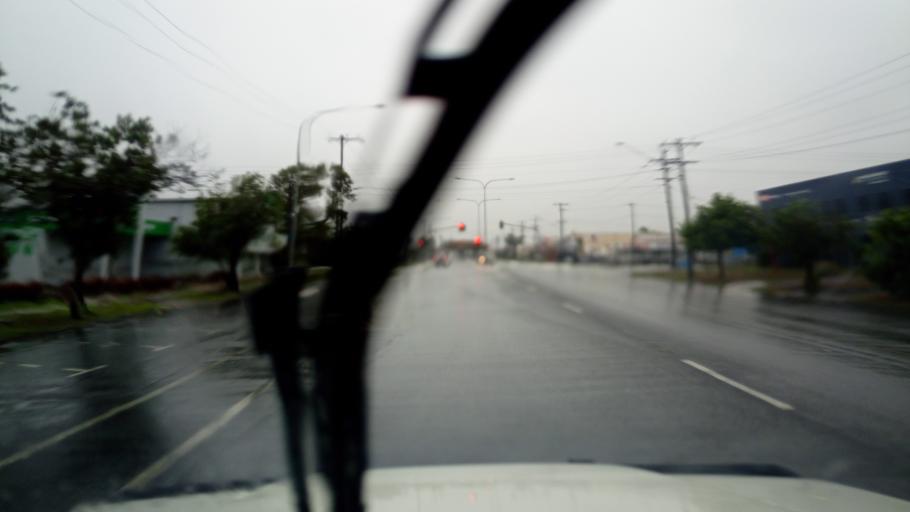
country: AU
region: Queensland
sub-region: Cairns
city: Woree
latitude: -16.9410
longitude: 145.7571
